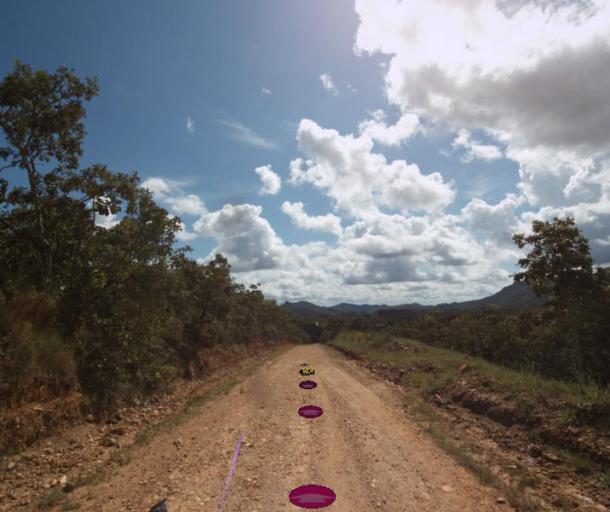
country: BR
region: Goias
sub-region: Pirenopolis
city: Pirenopolis
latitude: -15.7803
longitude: -48.9670
